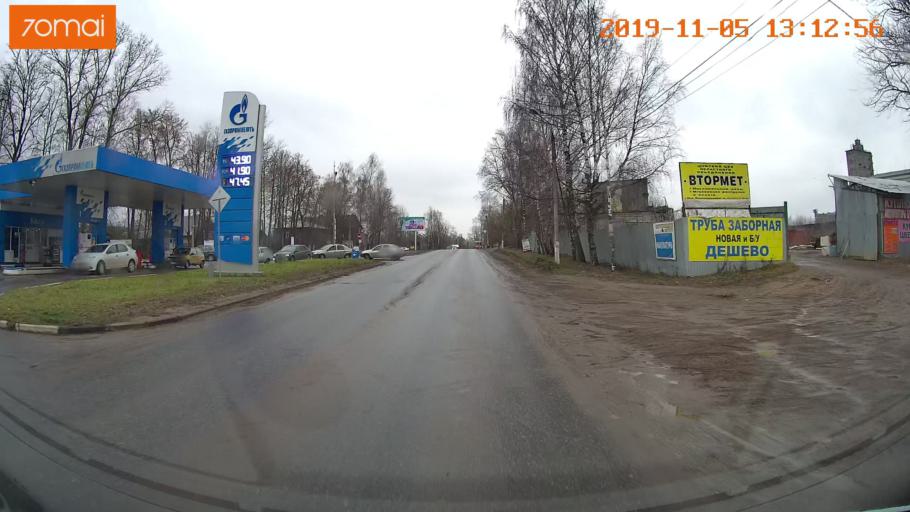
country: RU
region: Ivanovo
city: Shuya
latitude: 56.8544
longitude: 41.3532
